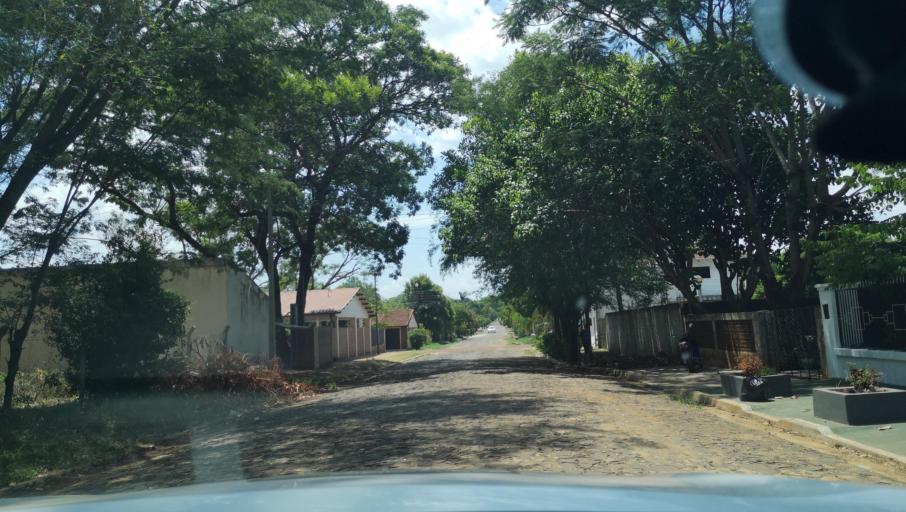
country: PY
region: Itapua
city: Carmen del Parana
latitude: -27.1643
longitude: -56.2358
